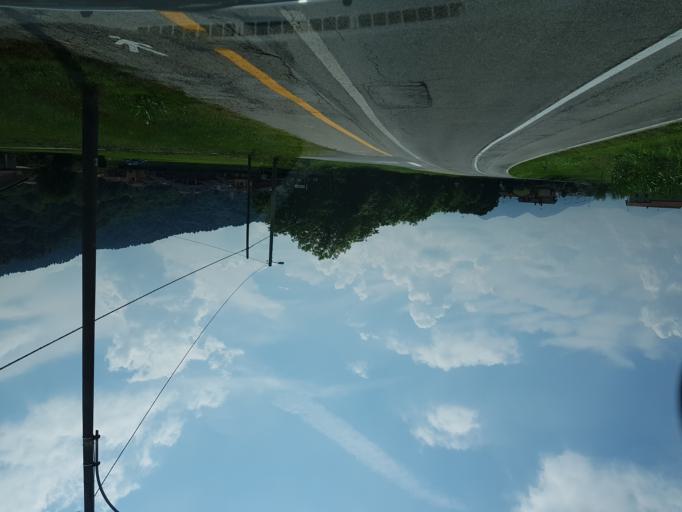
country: IT
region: Piedmont
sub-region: Provincia di Cuneo
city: Vignolo
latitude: 44.3668
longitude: 7.4740
